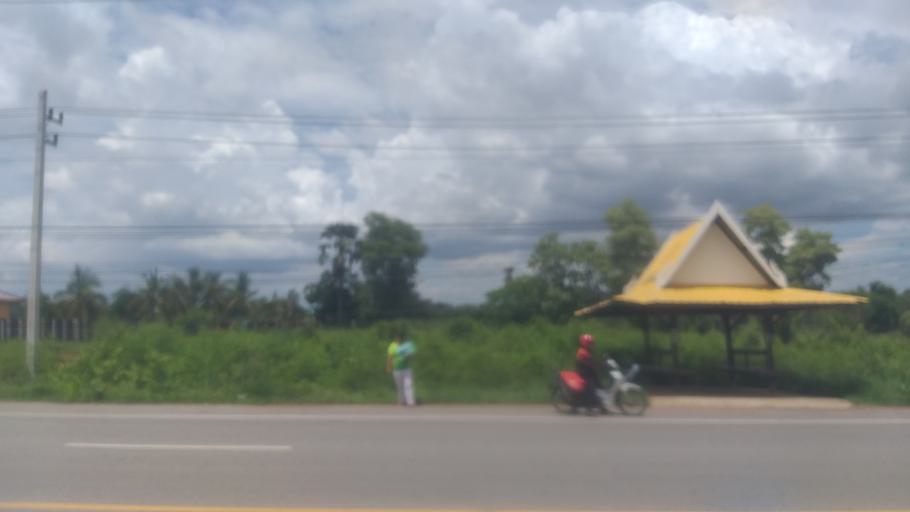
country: TH
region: Nakhon Ratchasima
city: Non Thai
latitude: 15.1320
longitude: 102.1041
